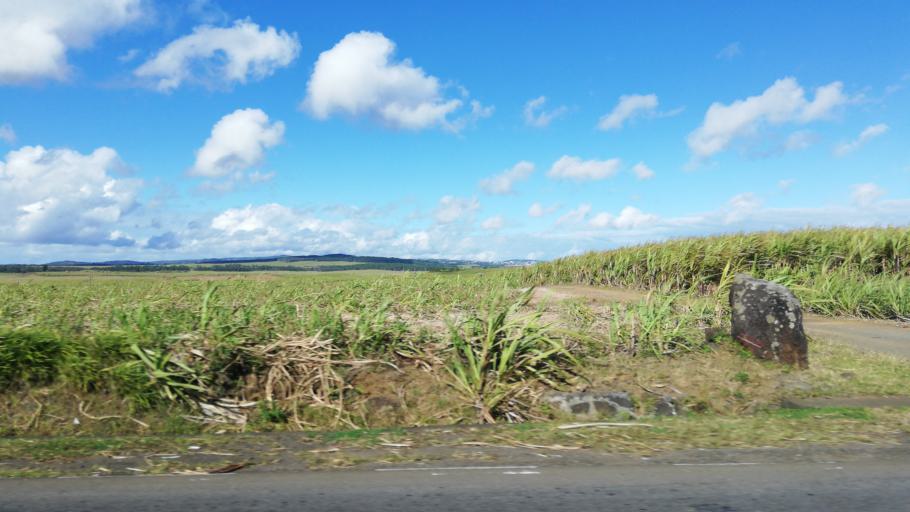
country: MU
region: Moka
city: Quartier Militaire
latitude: -20.2407
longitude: 57.5820
